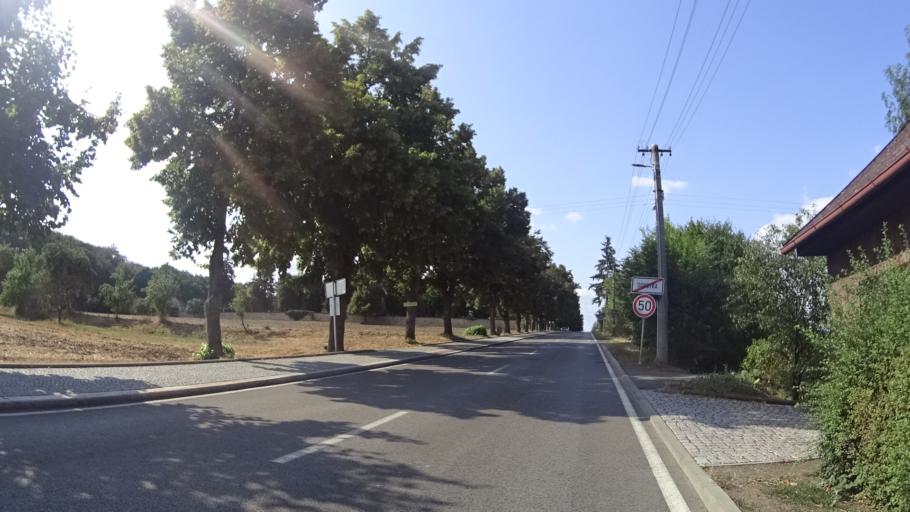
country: CZ
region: Kralovehradecky
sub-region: Okres Jicin
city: Sobotka
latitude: 50.4706
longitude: 15.1748
